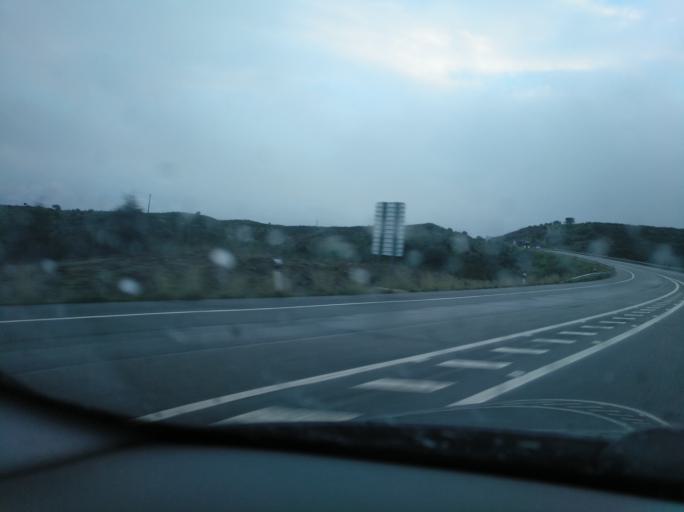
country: PT
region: Faro
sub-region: Castro Marim
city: Castro Marim
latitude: 37.3121
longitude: -7.4904
